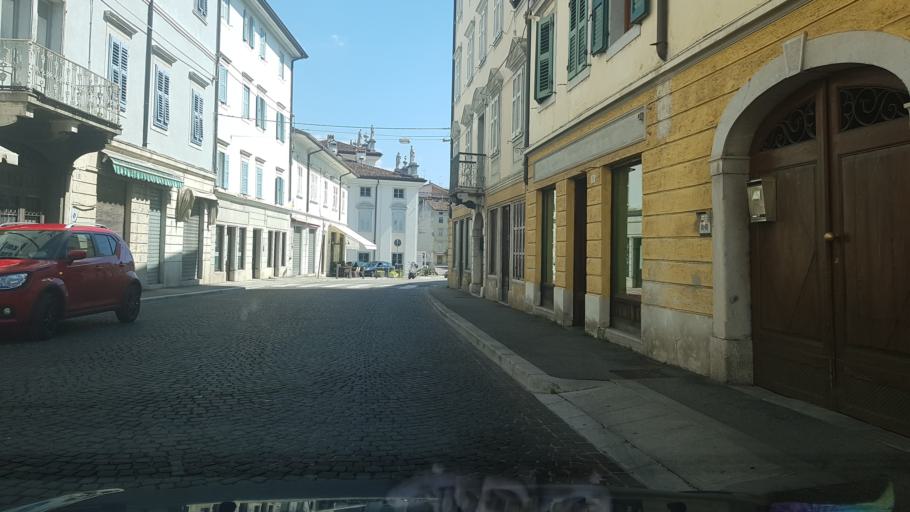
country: IT
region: Friuli Venezia Giulia
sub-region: Provincia di Gorizia
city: Gorizia
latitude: 45.9485
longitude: 13.6263
